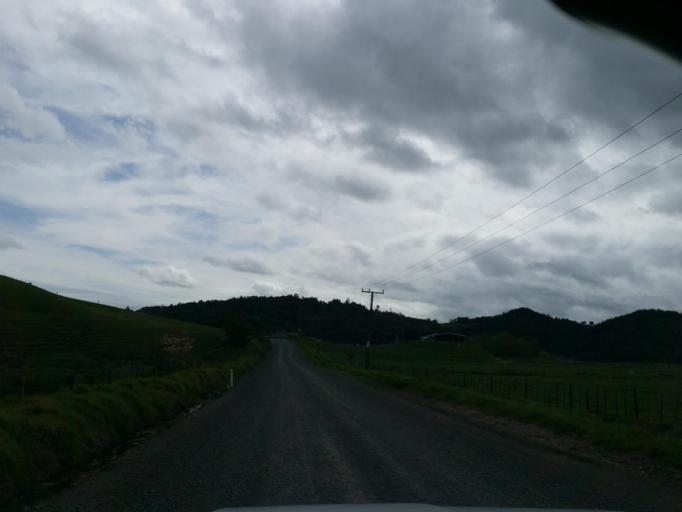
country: NZ
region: Northland
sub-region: Kaipara District
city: Dargaville
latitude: -35.8950
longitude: 173.9873
